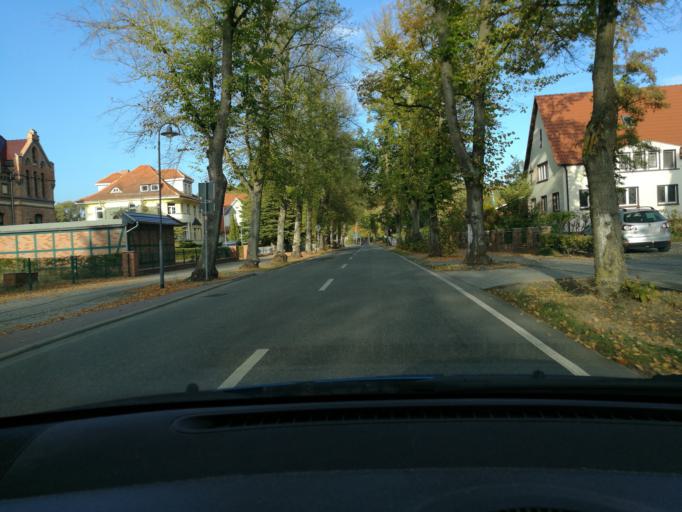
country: DE
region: Saxony-Anhalt
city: Luftkurort Arendsee
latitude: 52.8853
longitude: 11.4963
